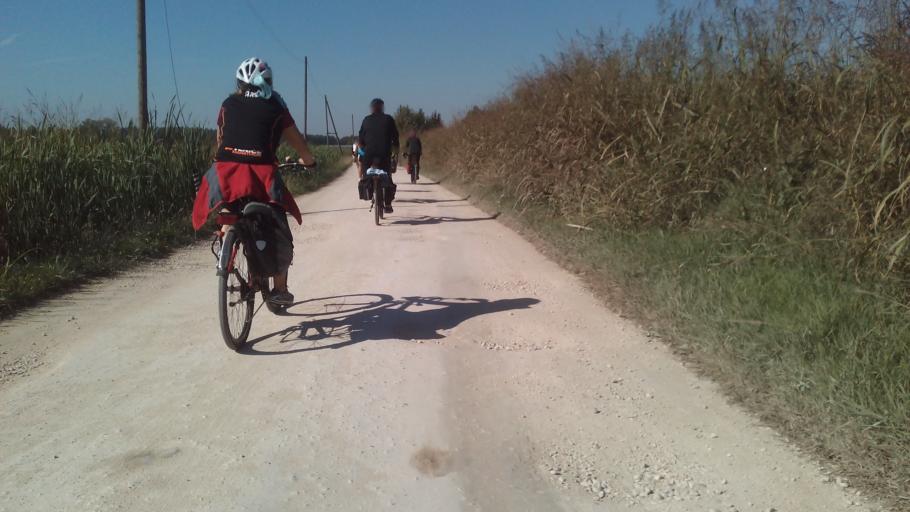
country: IT
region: Veneto
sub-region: Provincia di Verona
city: Isola della Scala
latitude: 45.2843
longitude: 10.9931
